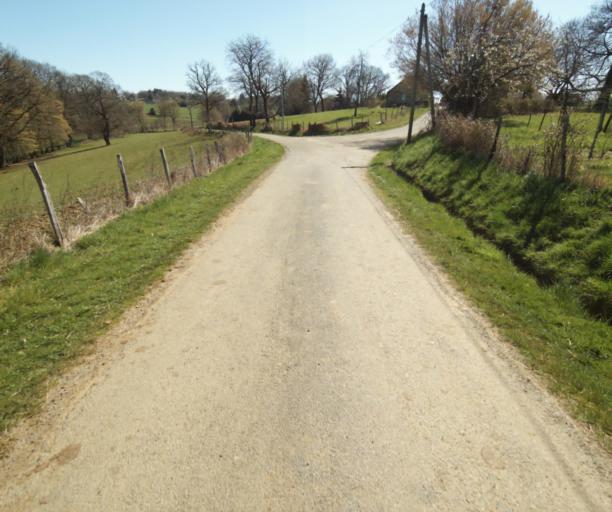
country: FR
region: Limousin
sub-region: Departement de la Correze
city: Uzerche
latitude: 45.4022
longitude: 1.6276
